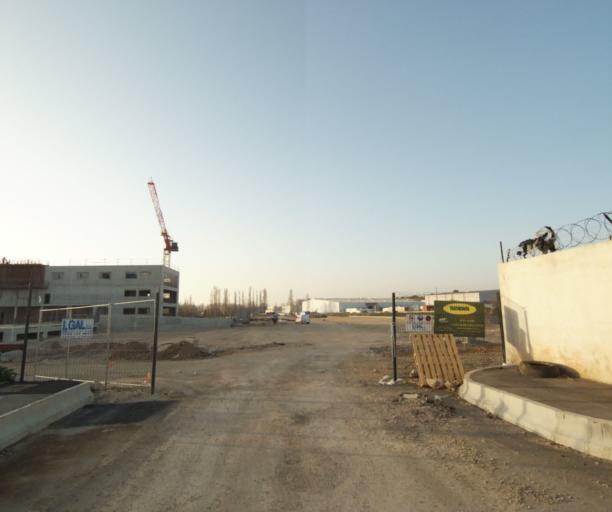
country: FR
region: Provence-Alpes-Cote d'Azur
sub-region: Departement des Bouches-du-Rhone
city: Saint-Victoret
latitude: 43.4197
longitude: 5.2628
